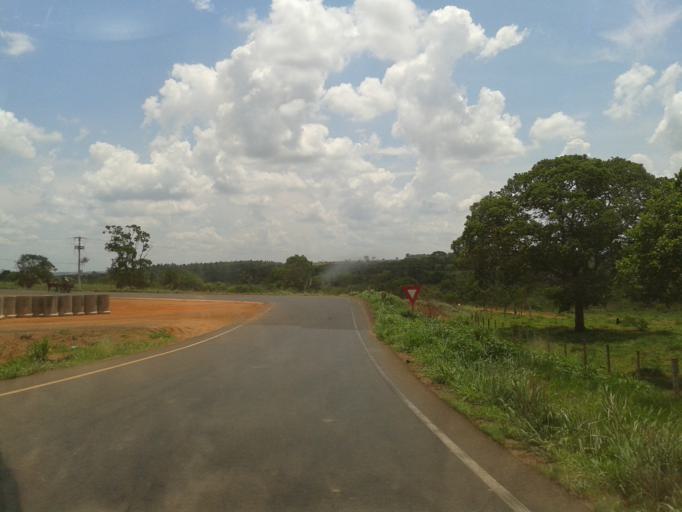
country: BR
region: Minas Gerais
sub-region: Monte Alegre De Minas
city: Monte Alegre de Minas
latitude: -18.8753
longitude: -48.8922
